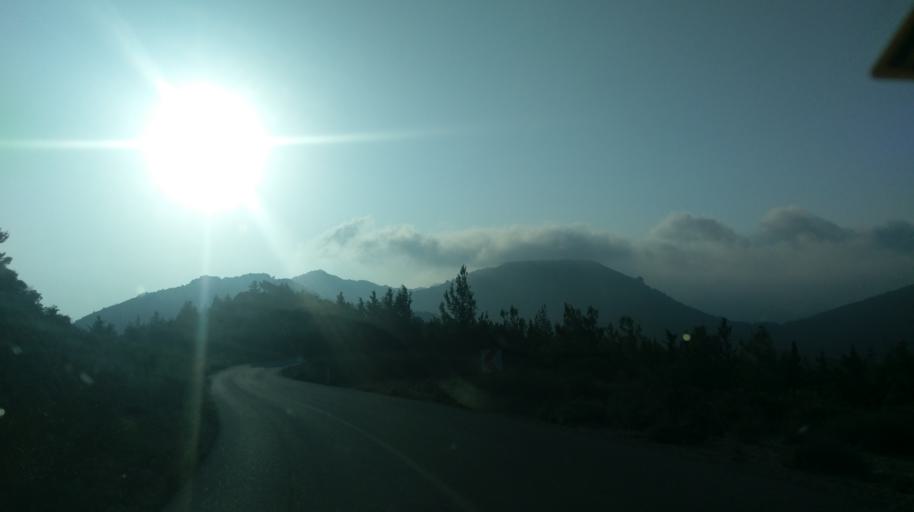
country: CY
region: Ammochostos
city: Trikomo
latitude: 35.3730
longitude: 33.8634
